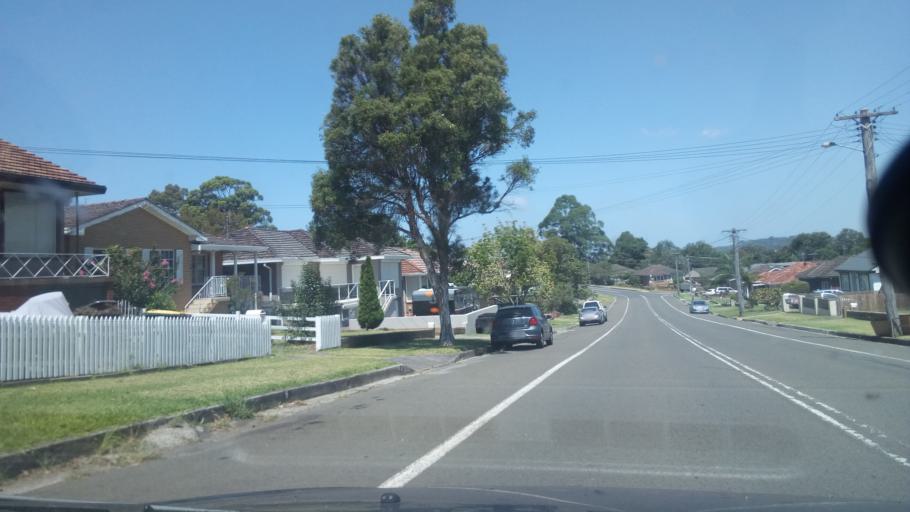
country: AU
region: New South Wales
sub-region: Wollongong
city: West Wollongong
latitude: -34.4284
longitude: 150.8629
